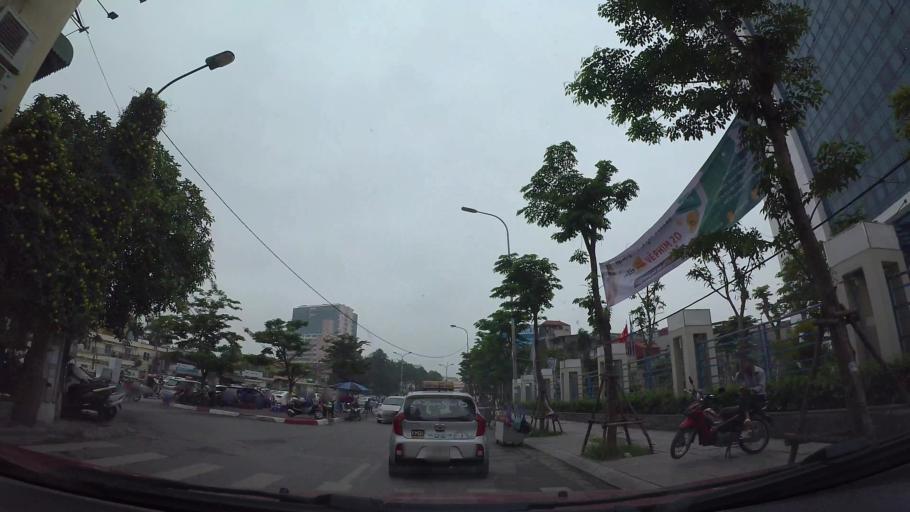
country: VN
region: Ha Noi
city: Hai BaTrung
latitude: 20.9998
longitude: 105.8417
